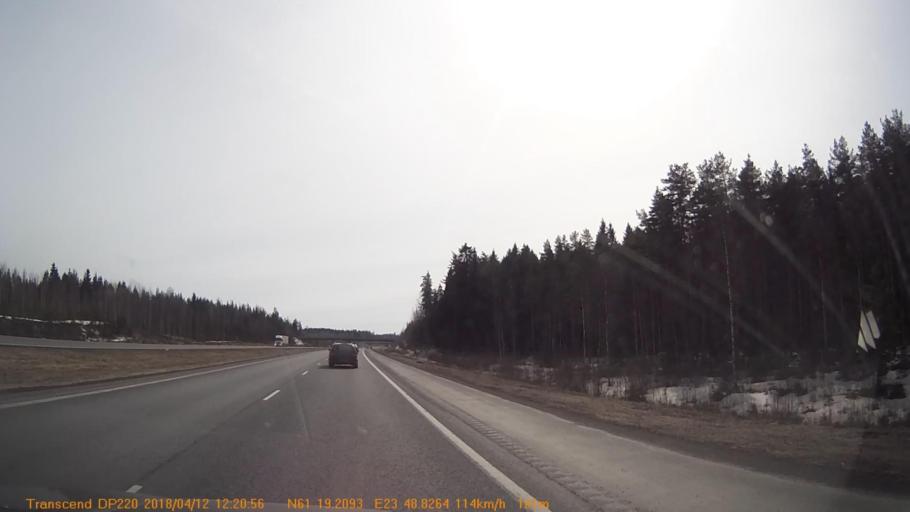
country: FI
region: Pirkanmaa
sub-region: Tampere
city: Lempaeaelae
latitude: 61.3197
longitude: 23.8143
